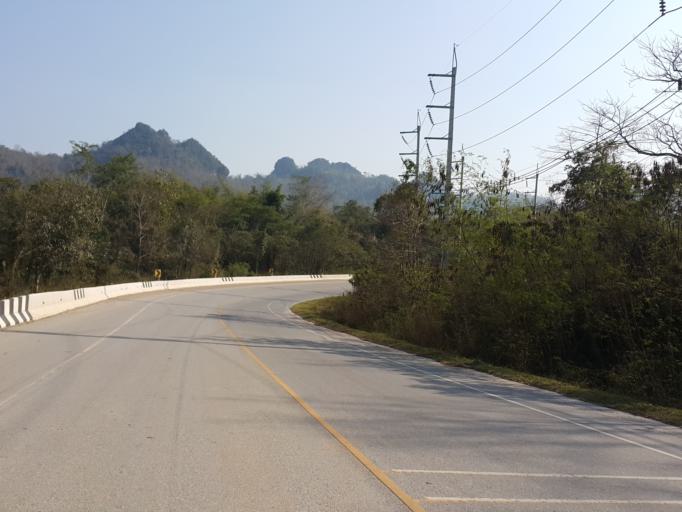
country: TH
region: Lampang
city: Chae Hom
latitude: 18.5490
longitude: 99.5685
